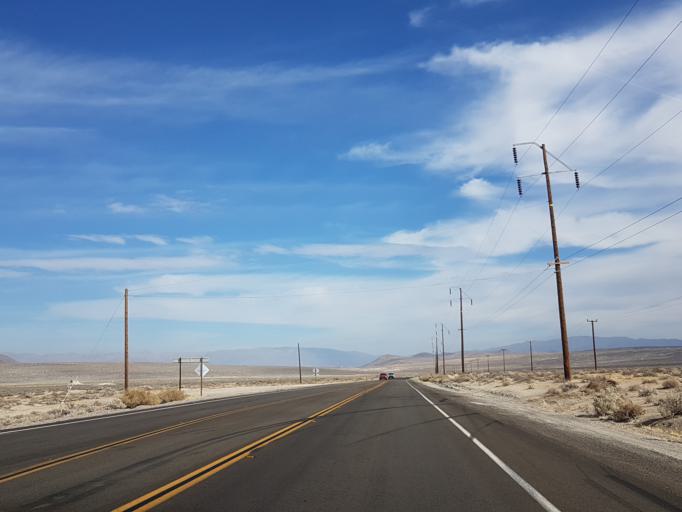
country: US
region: California
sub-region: San Bernardino County
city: Searles Valley
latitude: 35.6471
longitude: -117.5096
